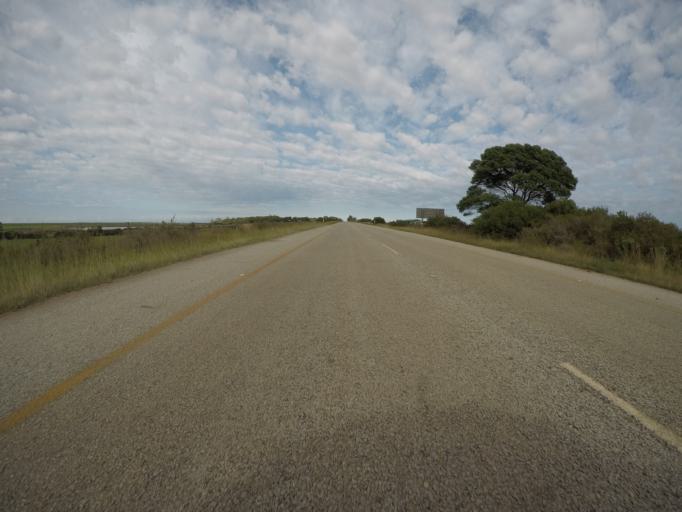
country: ZA
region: Eastern Cape
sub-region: Cacadu District Municipality
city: Kareedouw
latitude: -34.0484
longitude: 24.4570
